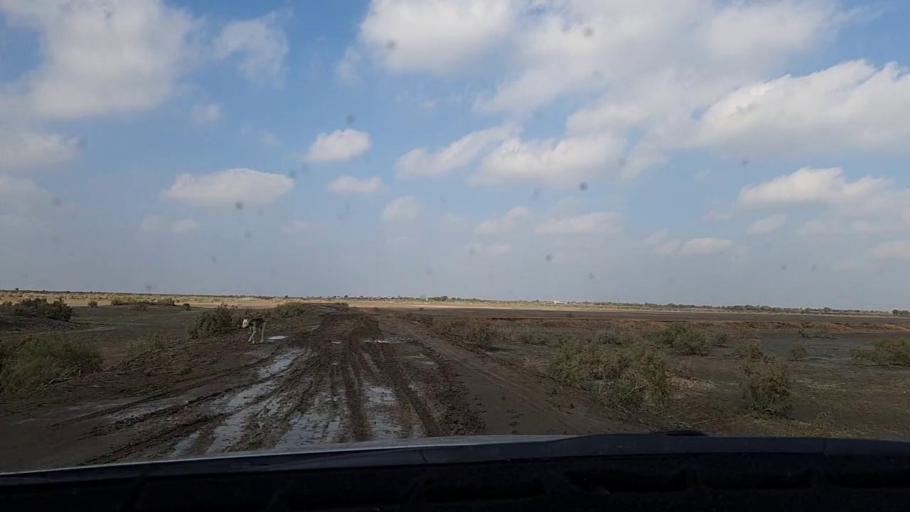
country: PK
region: Sindh
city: Tando Mittha Khan
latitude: 25.7869
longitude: 69.2560
